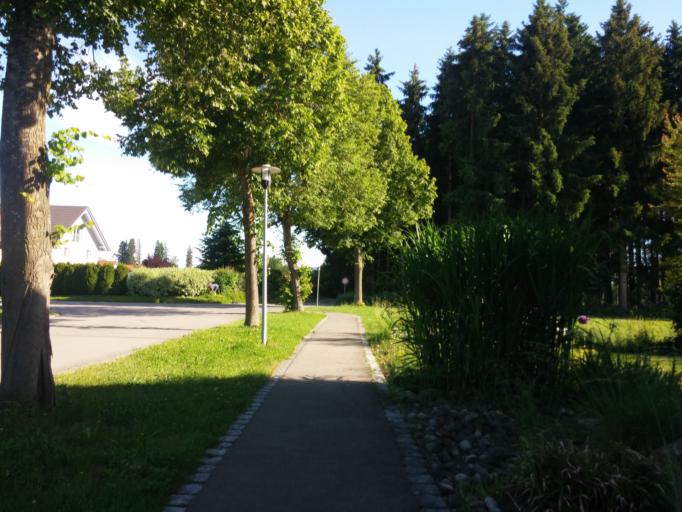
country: DE
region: Baden-Wuerttemberg
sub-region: Tuebingen Region
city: Berkheim
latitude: 48.0376
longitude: 10.0783
